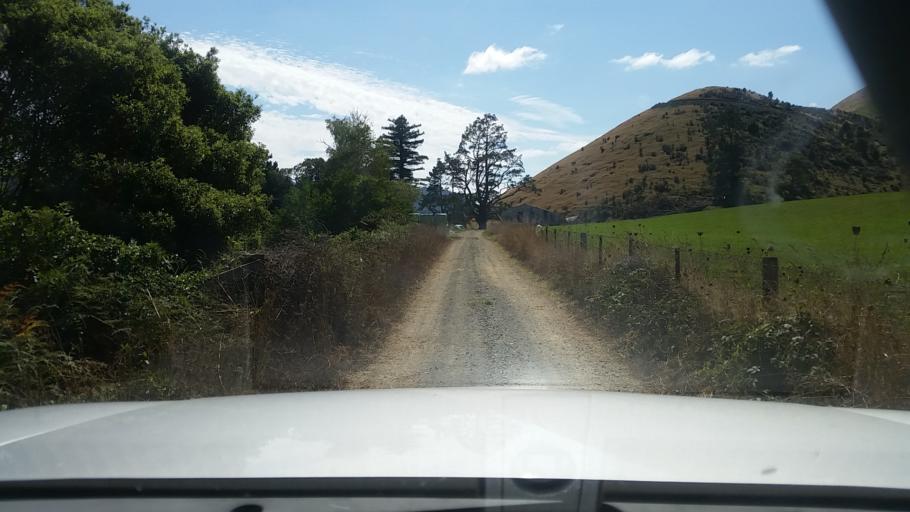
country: NZ
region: Nelson
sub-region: Nelson City
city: Nelson
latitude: -41.2483
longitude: 173.5854
